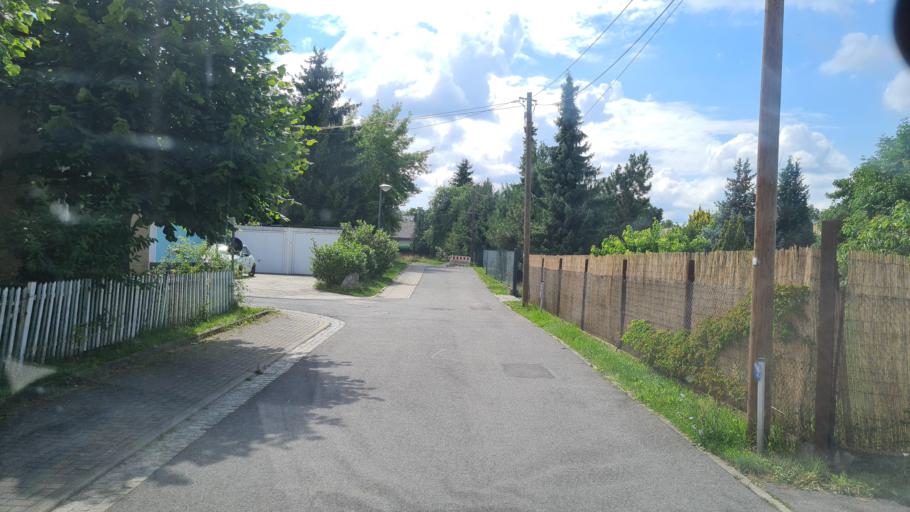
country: DE
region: Brandenburg
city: Schipkau
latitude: 51.5401
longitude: 13.8915
